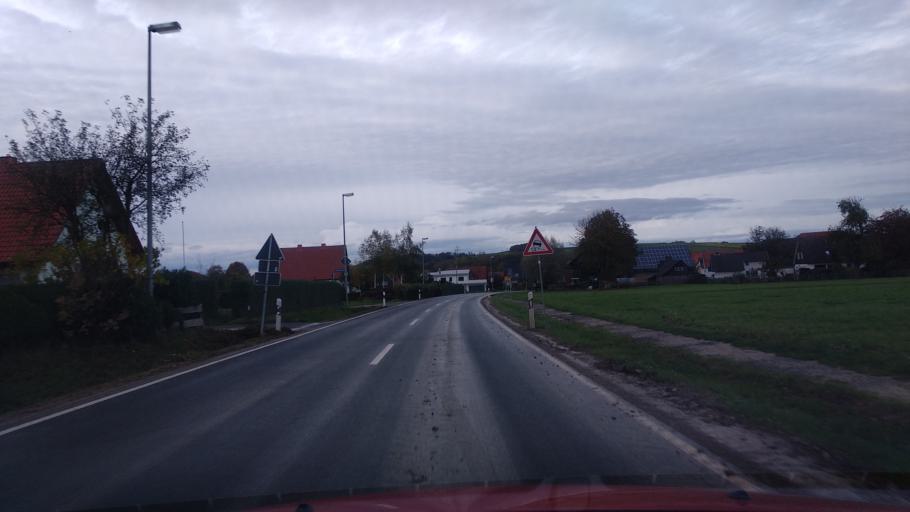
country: DE
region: North Rhine-Westphalia
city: Brakel
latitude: 51.6855
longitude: 9.2252
